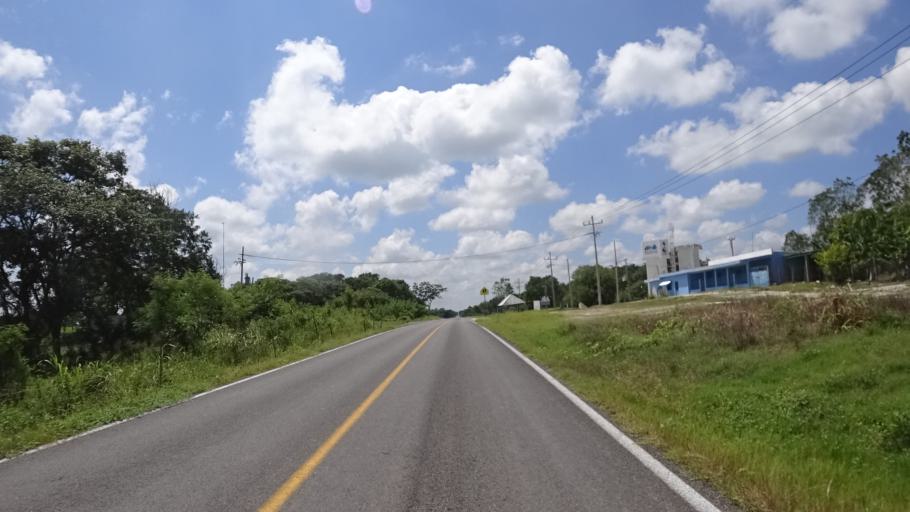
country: MX
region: Campeche
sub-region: Carmen
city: Licenciado Gustavo Diaz Ordaz (18 de Marzo)
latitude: 18.6968
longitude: -90.9751
